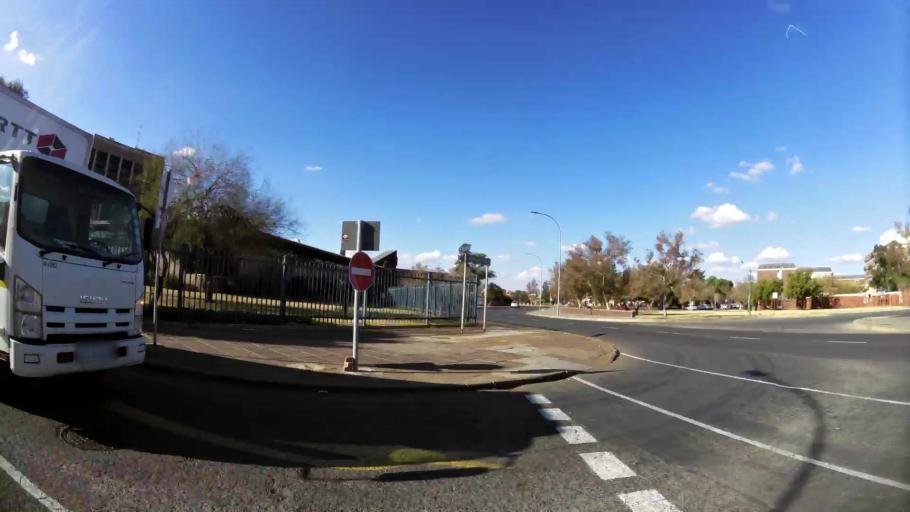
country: ZA
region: Northern Cape
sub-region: Frances Baard District Municipality
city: Kimberley
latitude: -28.7460
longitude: 24.7649
